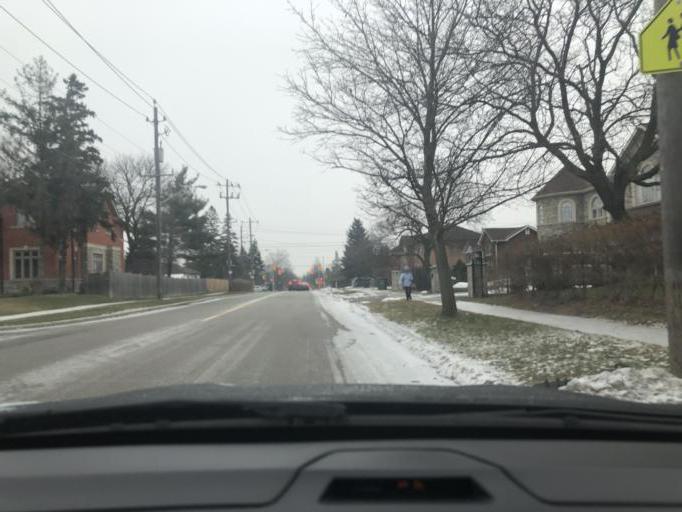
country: CA
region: Ontario
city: Scarborough
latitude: 43.7831
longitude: -79.2680
